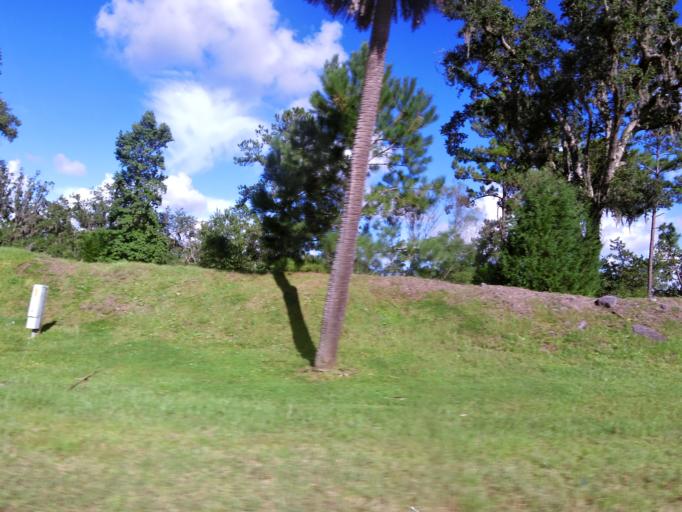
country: US
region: Georgia
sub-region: Camden County
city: Woodbine
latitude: 31.0806
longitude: -81.7266
